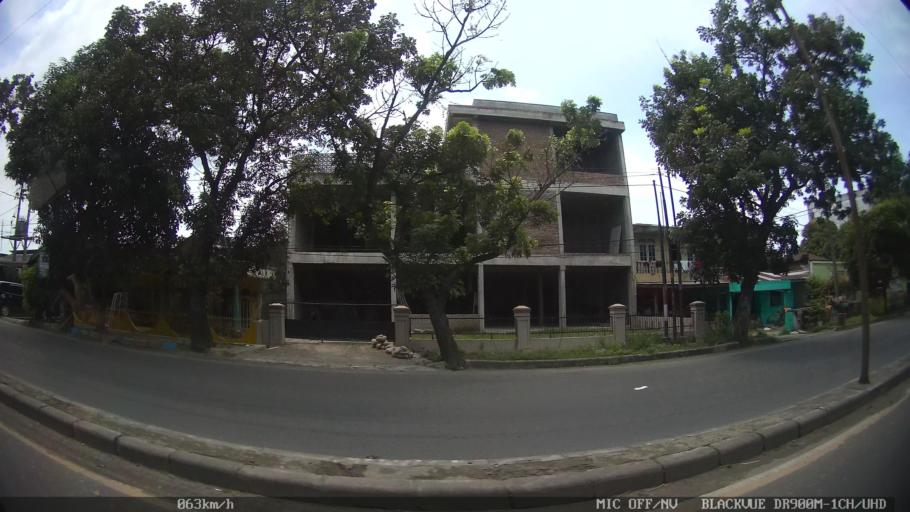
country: ID
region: North Sumatra
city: Labuhan Deli
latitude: 3.7054
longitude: 98.6791
